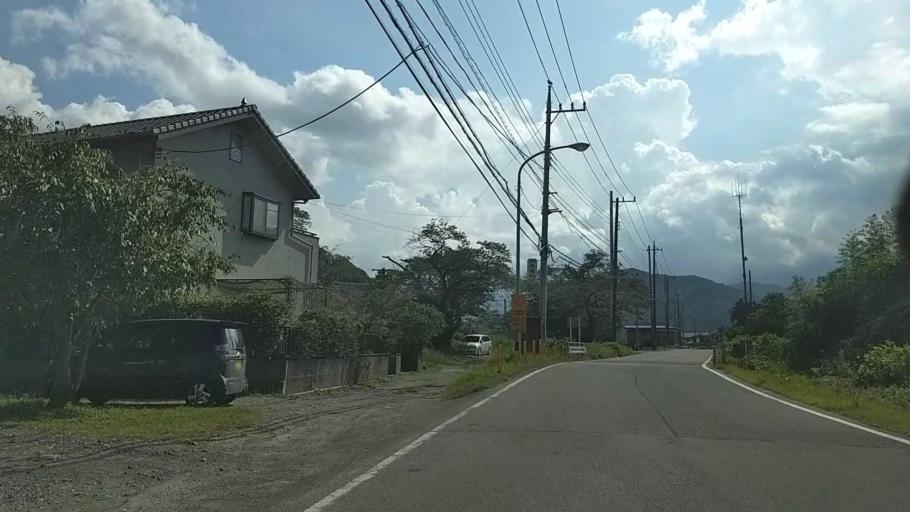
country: JP
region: Shizuoka
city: Fujinomiya
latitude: 35.3803
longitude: 138.4541
